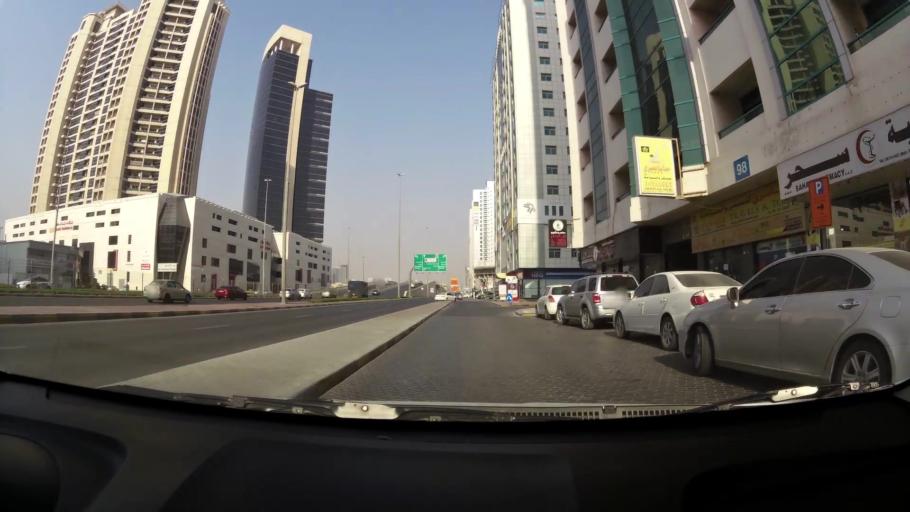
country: AE
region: Ajman
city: Ajman
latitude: 25.3922
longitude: 55.4374
